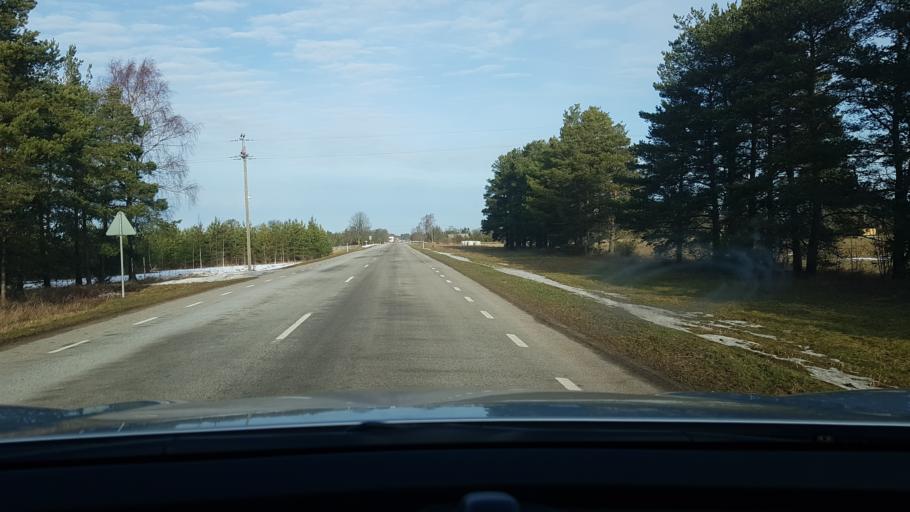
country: EE
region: Saare
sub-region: Kuressaare linn
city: Kuressaare
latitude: 58.5151
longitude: 22.7044
